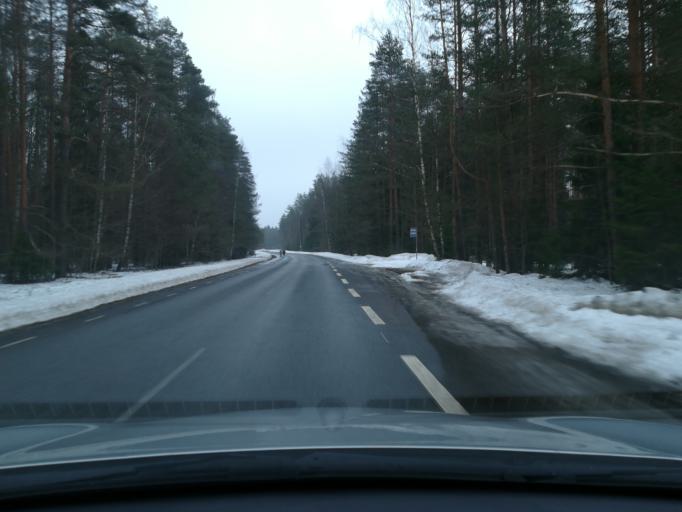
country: EE
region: Harju
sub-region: Loksa linn
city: Loksa
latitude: 59.4757
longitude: 25.6091
